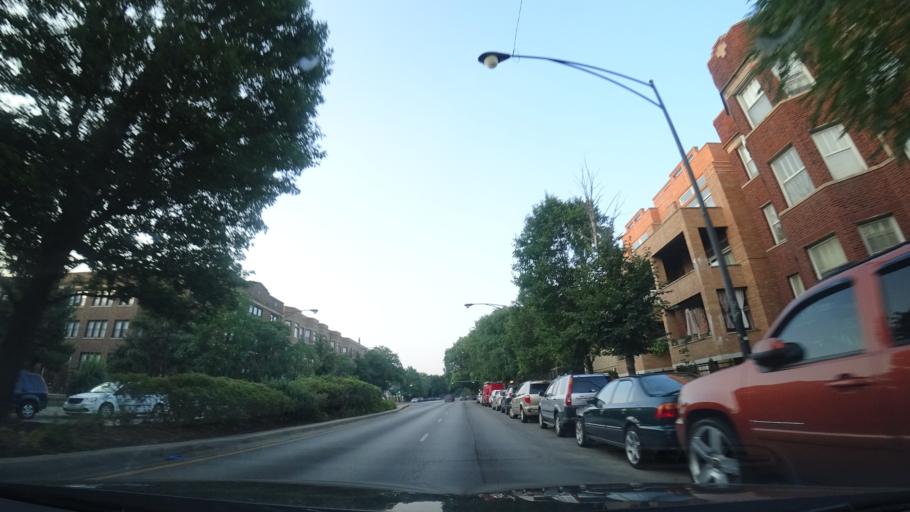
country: US
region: Illinois
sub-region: Cook County
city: Lincolnwood
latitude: 41.9662
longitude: -87.6695
